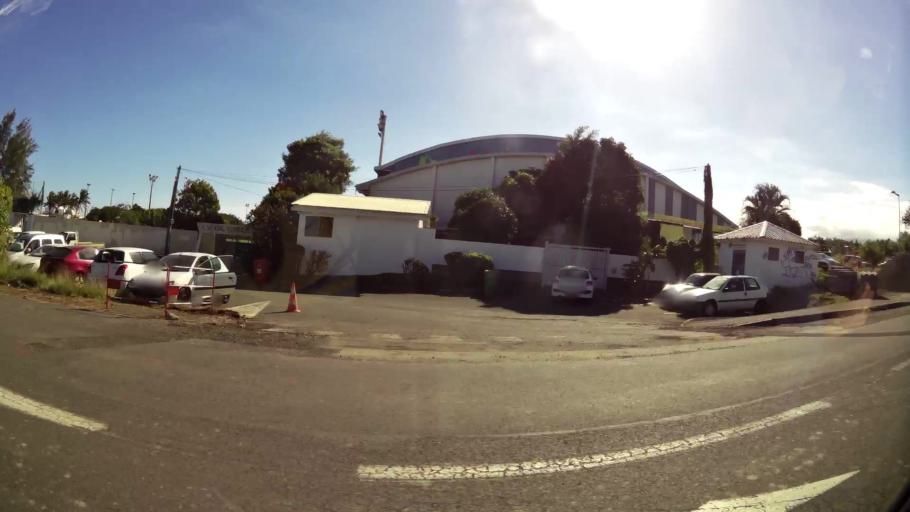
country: RE
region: Reunion
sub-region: Reunion
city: Saint-Pierre
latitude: -21.3440
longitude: 55.4927
